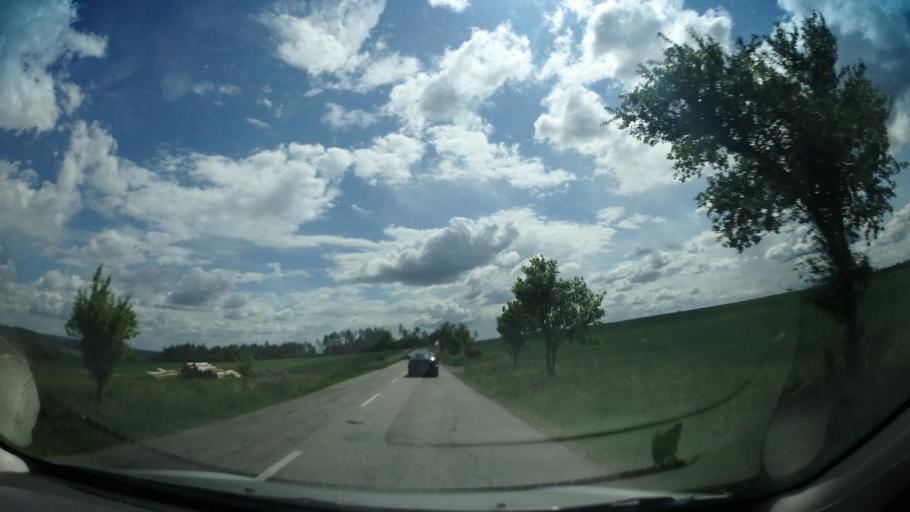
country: CZ
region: South Moravian
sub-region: Okres Blansko
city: Letovice
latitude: 49.5764
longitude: 16.5846
